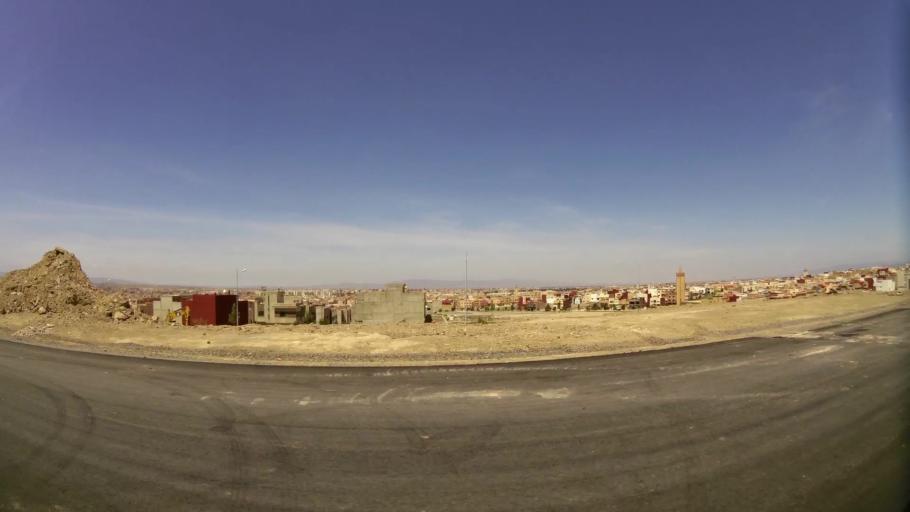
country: MA
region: Oriental
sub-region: Oujda-Angad
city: Oujda
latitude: 34.6509
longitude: -1.9212
